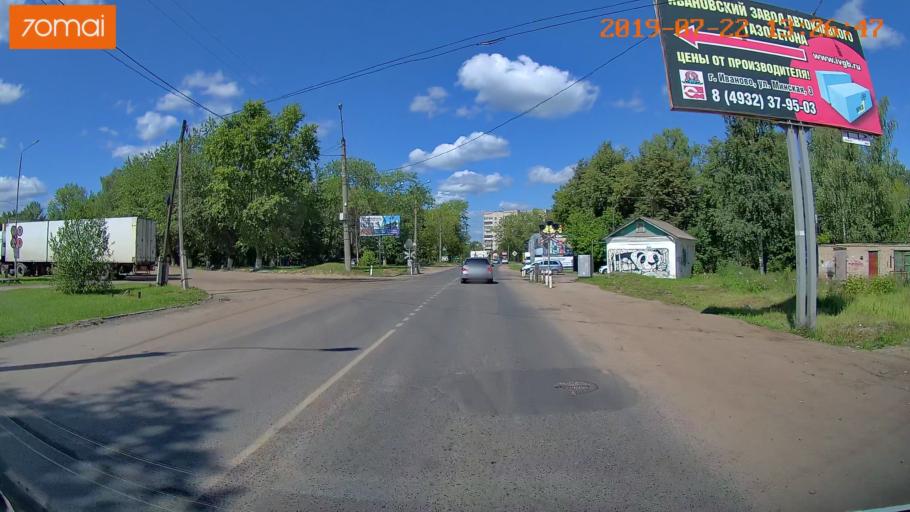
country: RU
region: Ivanovo
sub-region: Gorod Ivanovo
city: Ivanovo
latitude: 57.0303
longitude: 40.9481
